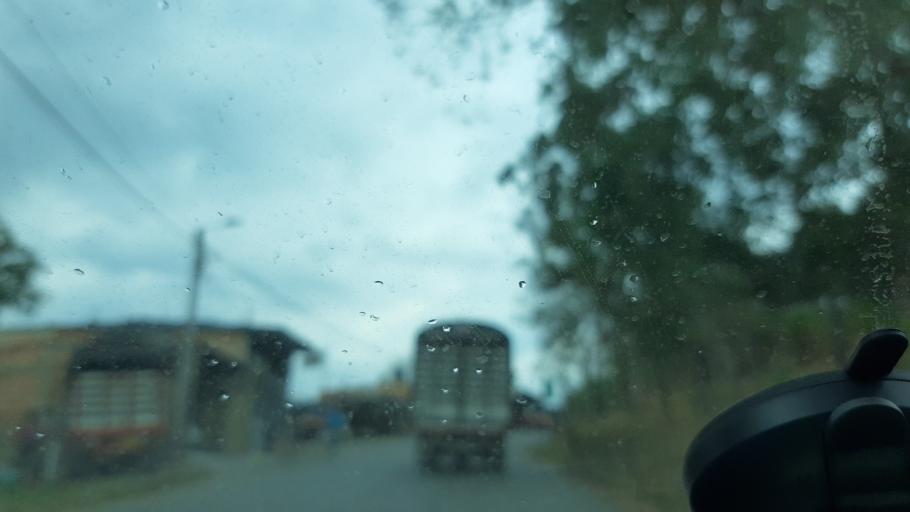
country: CO
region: Boyaca
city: Garagoa
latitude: 5.0785
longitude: -73.3697
